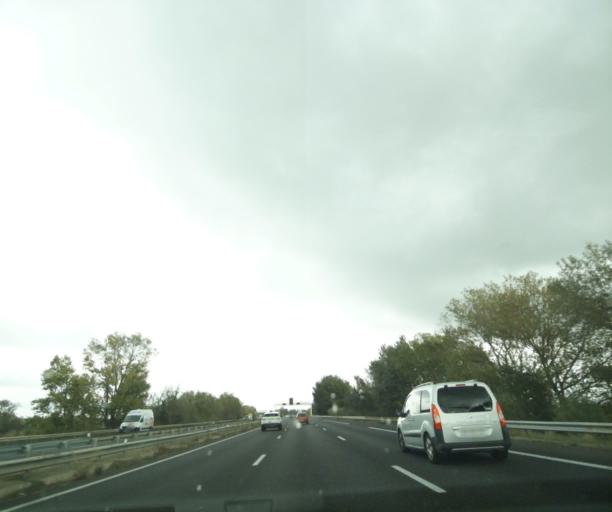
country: FR
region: Languedoc-Roussillon
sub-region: Departement de l'Herault
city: Sauvian
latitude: 43.3081
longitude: 3.2453
